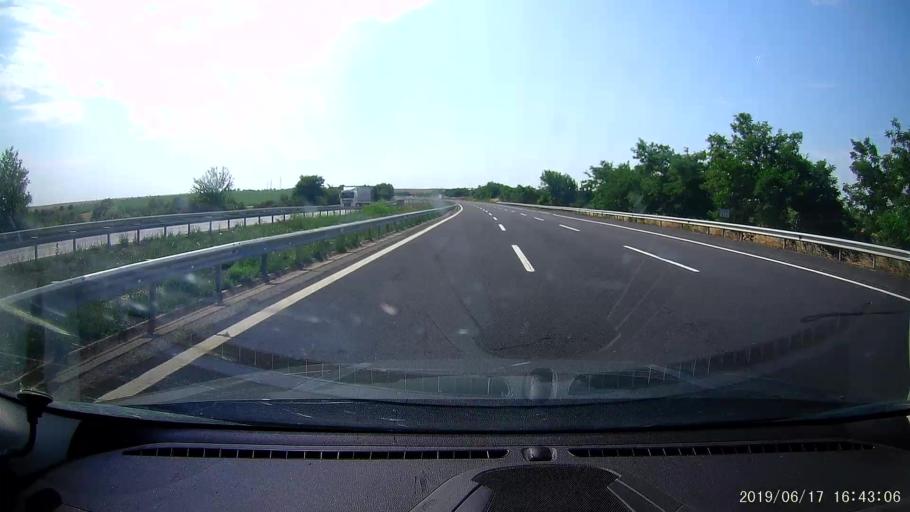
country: TR
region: Kirklareli
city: Luleburgaz
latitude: 41.4787
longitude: 27.3036
